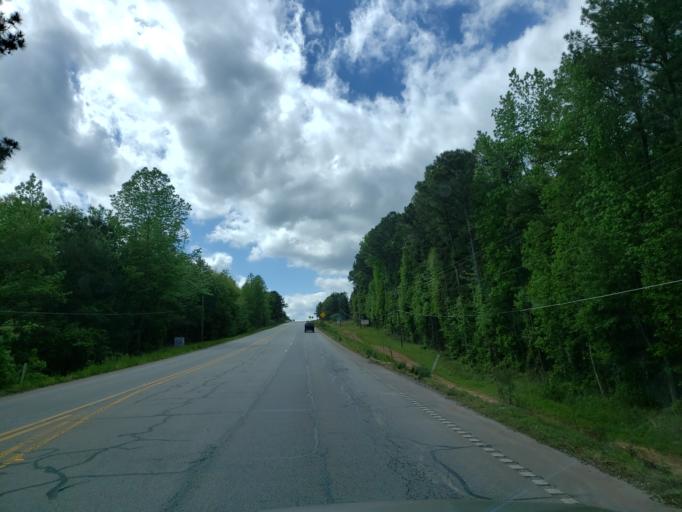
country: US
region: Georgia
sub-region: Haralson County
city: Bremen
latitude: 33.7114
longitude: -85.2087
